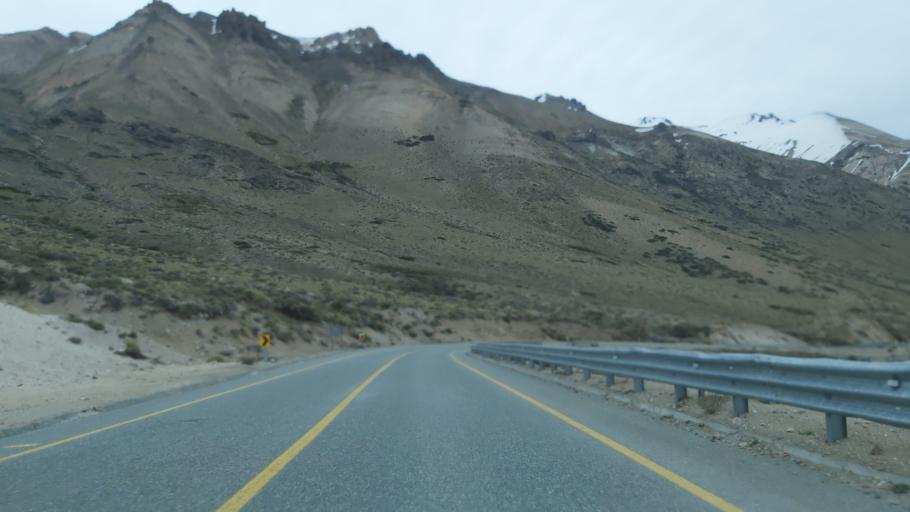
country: CL
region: Maule
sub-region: Provincia de Linares
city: Colbun
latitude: -35.9548
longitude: -70.5869
